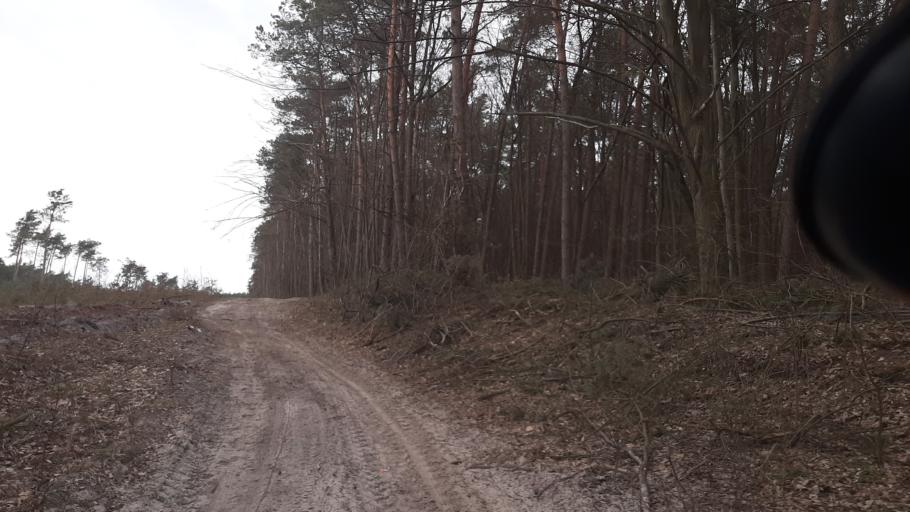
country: PL
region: Lublin Voivodeship
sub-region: Powiat lubelski
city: Garbow
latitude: 51.3943
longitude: 22.3794
